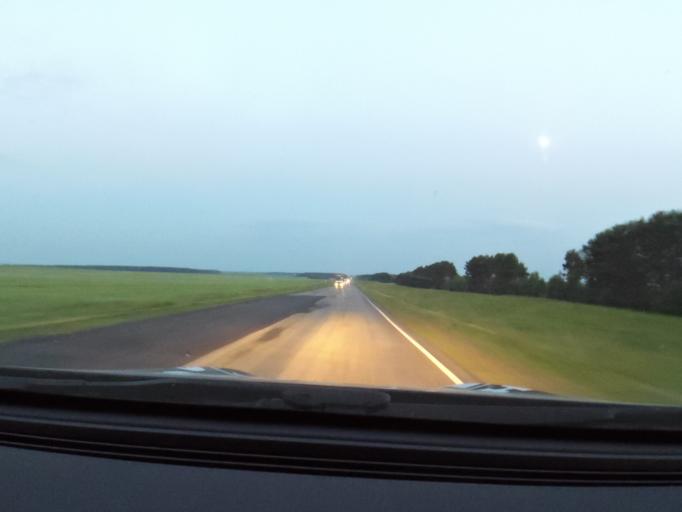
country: RU
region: Bashkortostan
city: Duvan
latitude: 56.1092
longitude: 58.0549
